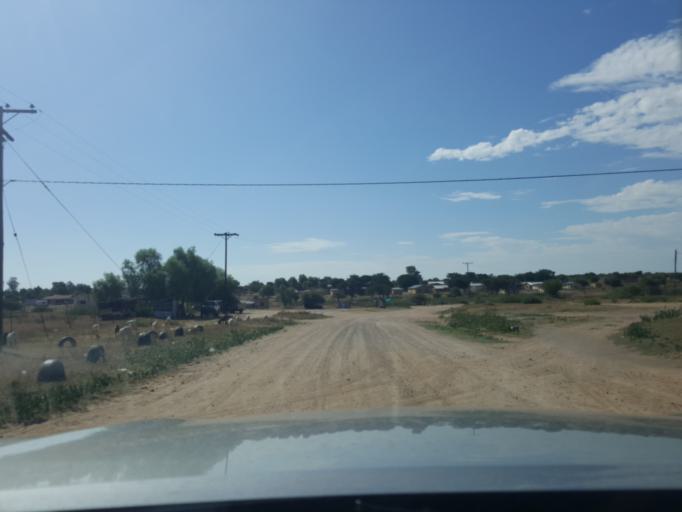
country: BW
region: Kweneng
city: Khudumelapye
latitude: -23.6967
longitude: 24.7180
